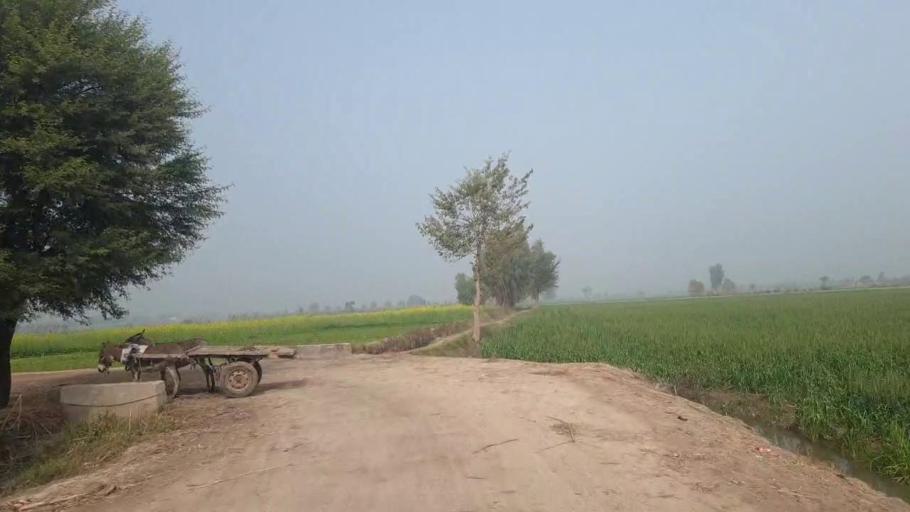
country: PK
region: Sindh
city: Bhit Shah
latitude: 25.8230
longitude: 68.5564
